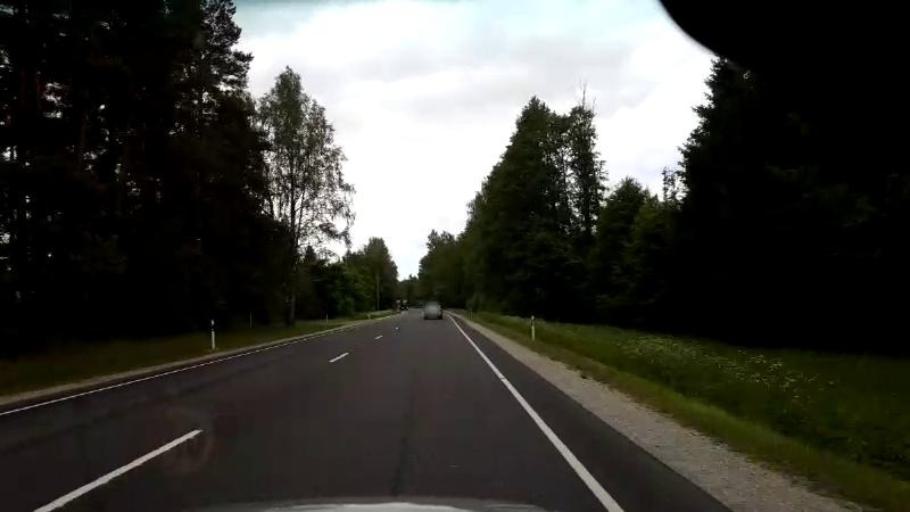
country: EE
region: Paernumaa
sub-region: Paernu linn
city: Parnu
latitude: 58.2471
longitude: 24.5176
